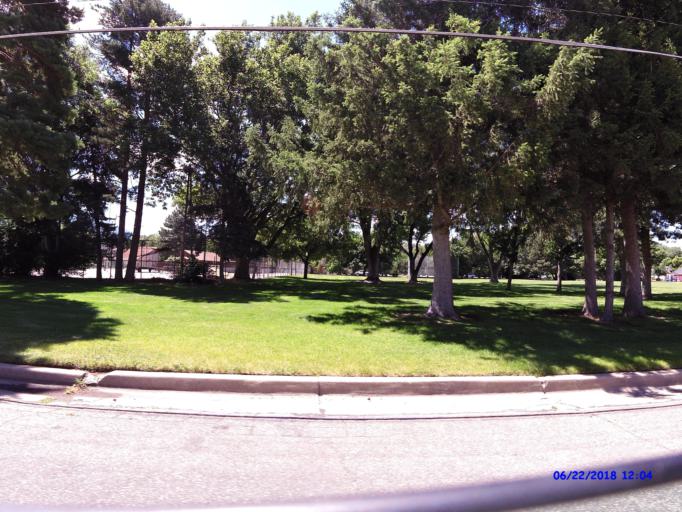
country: US
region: Utah
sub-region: Weber County
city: Ogden
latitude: 41.2376
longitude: -111.9635
